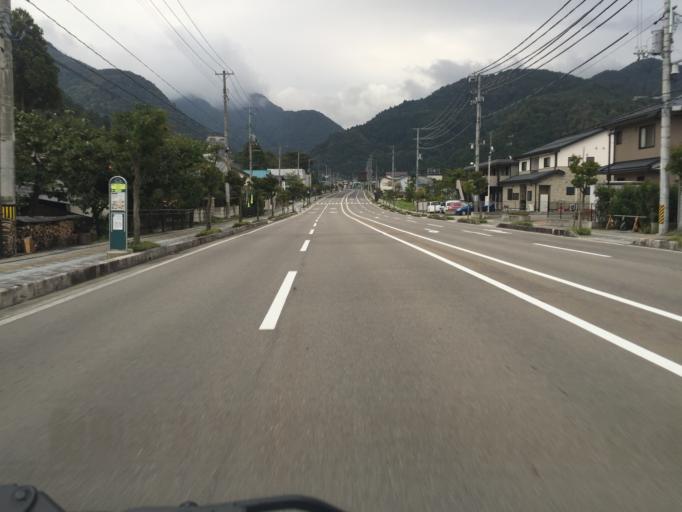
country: JP
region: Fukushima
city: Kitakata
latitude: 37.4878
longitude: 139.9503
